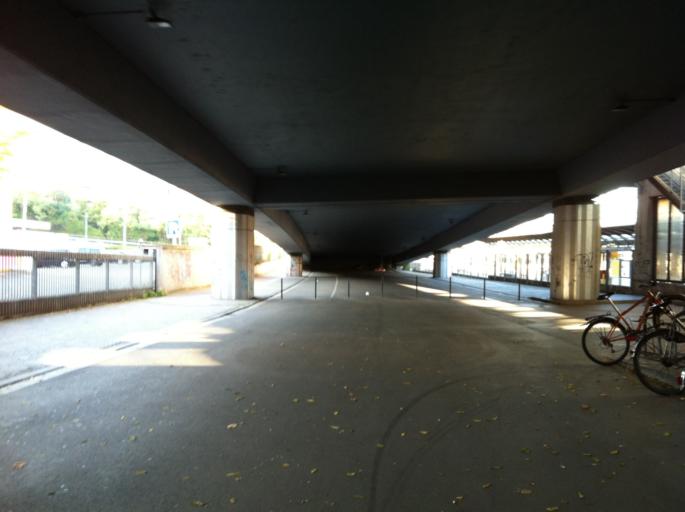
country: DE
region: Rheinland-Pfalz
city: Mainz
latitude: 50.0010
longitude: 8.2573
